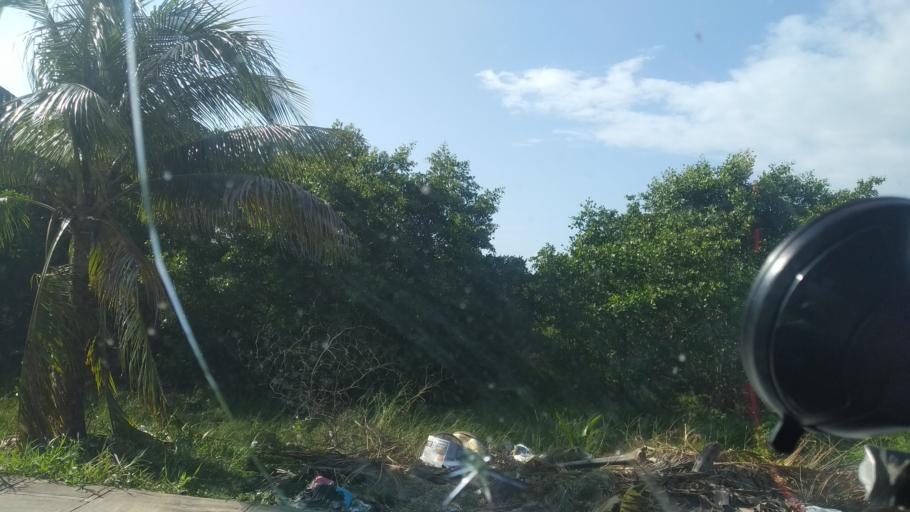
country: BZ
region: Belize
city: Belize City
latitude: 17.4843
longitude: -88.2074
